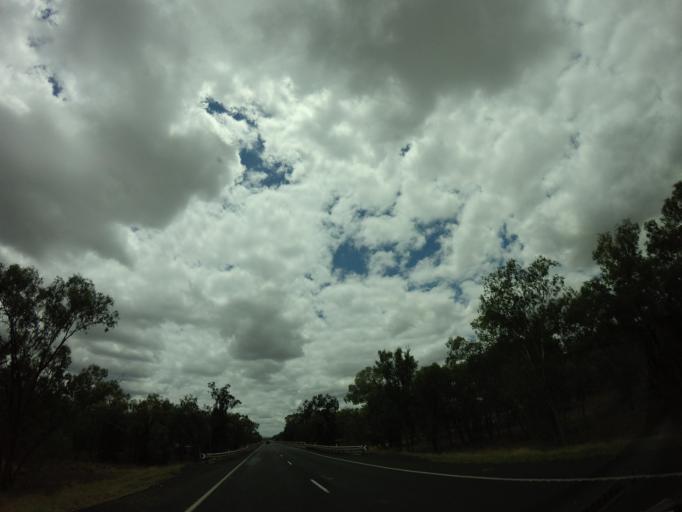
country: AU
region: Queensland
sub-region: Goondiwindi
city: Goondiwindi
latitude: -28.4007
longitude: 150.3087
